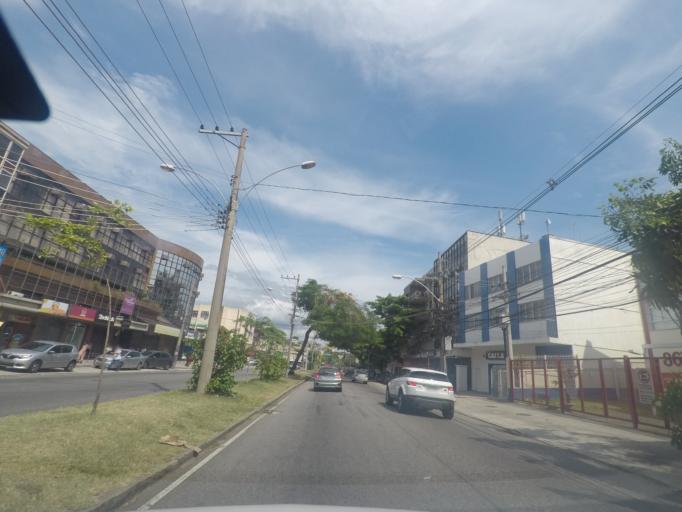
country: BR
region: Rio de Janeiro
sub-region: Rio De Janeiro
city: Rio de Janeiro
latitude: -22.8113
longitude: -43.1935
